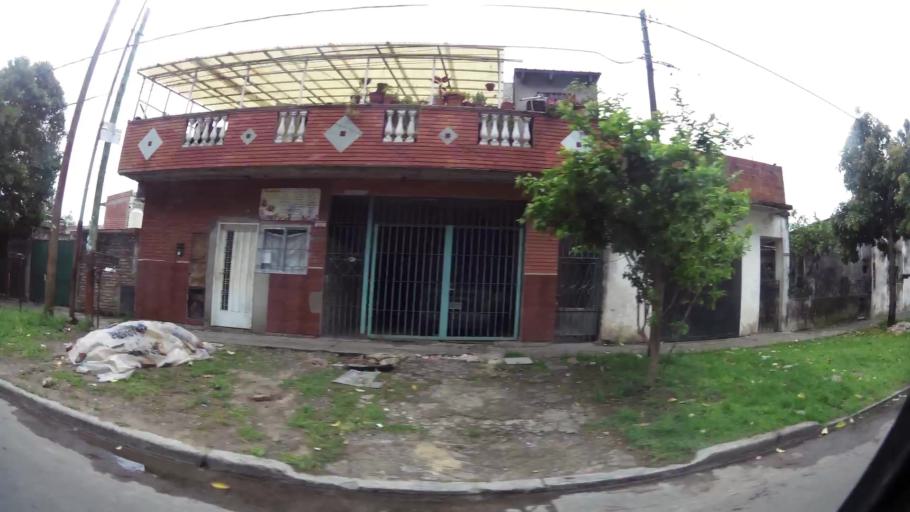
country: AR
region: Buenos Aires
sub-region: Partido de Lanus
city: Lanus
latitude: -34.7351
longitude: -58.3594
